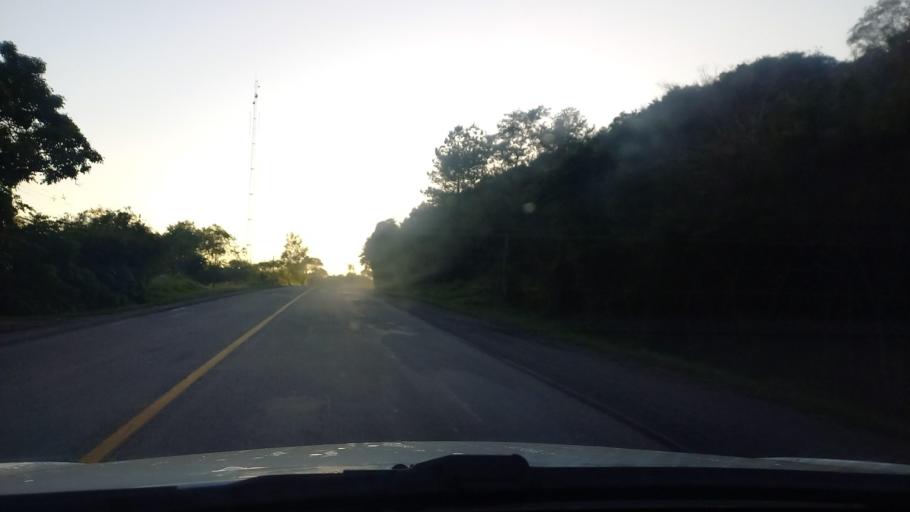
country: BR
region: Rio Grande do Sul
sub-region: Candelaria
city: Candelaria
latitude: -29.6827
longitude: -52.8436
